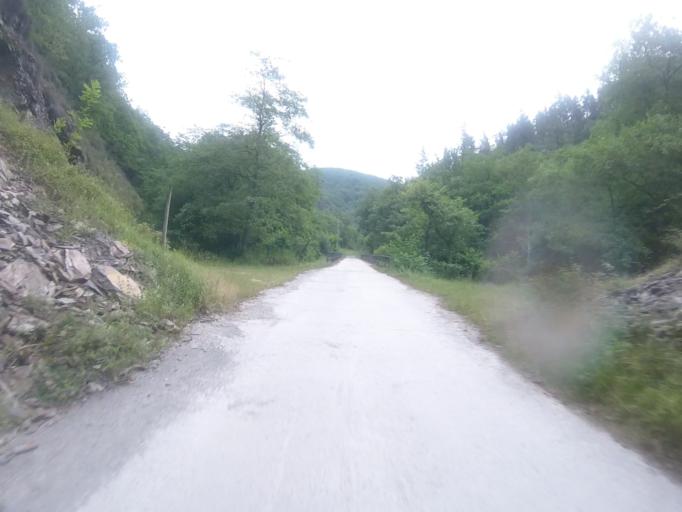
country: ES
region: Navarre
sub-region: Provincia de Navarra
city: Areso
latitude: 43.1172
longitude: -1.9373
